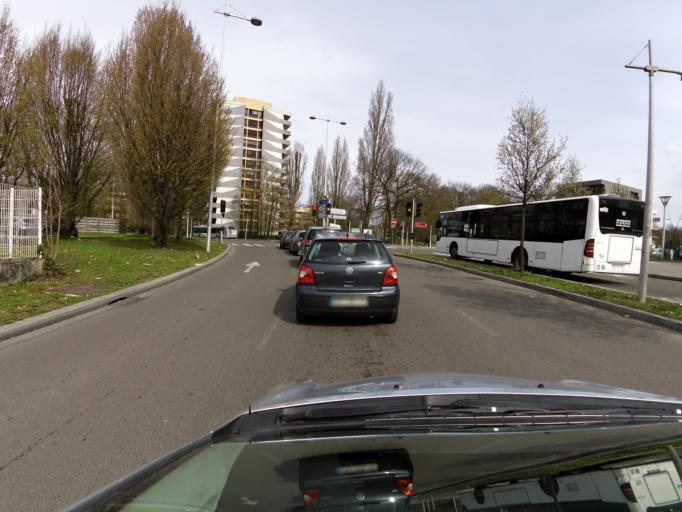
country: FR
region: Ile-de-France
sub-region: Departement de Seine-Saint-Denis
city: Tremblay-en-France
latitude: 48.9455
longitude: 2.5684
